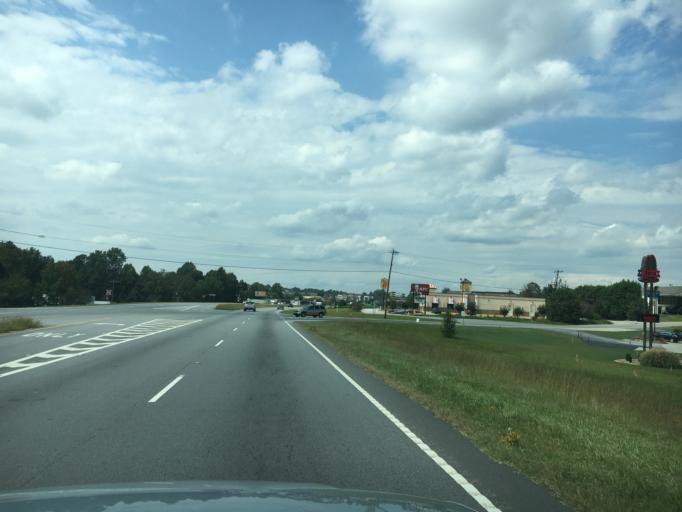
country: US
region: South Carolina
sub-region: Anderson County
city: Powdersville
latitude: 34.7777
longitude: -82.4675
